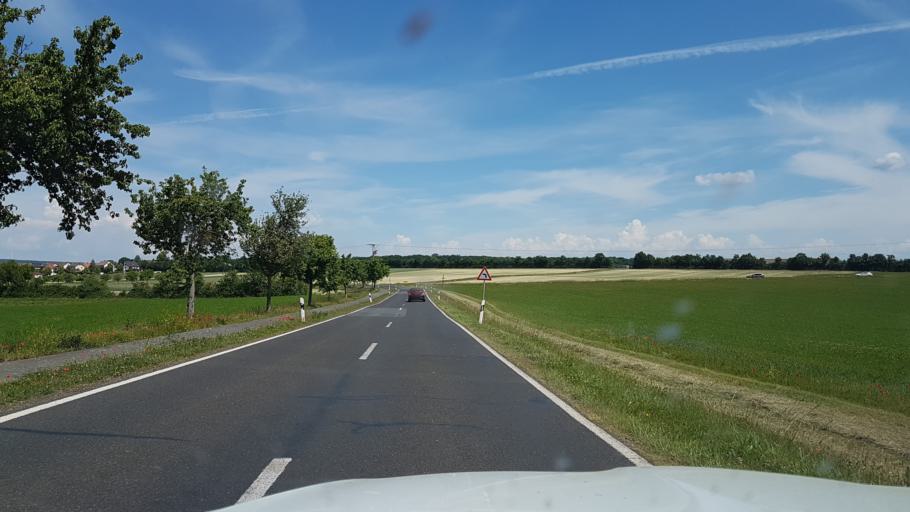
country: DE
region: Bavaria
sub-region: Regierungsbezirk Unterfranken
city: Knetzgau
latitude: 49.9918
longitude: 10.5079
